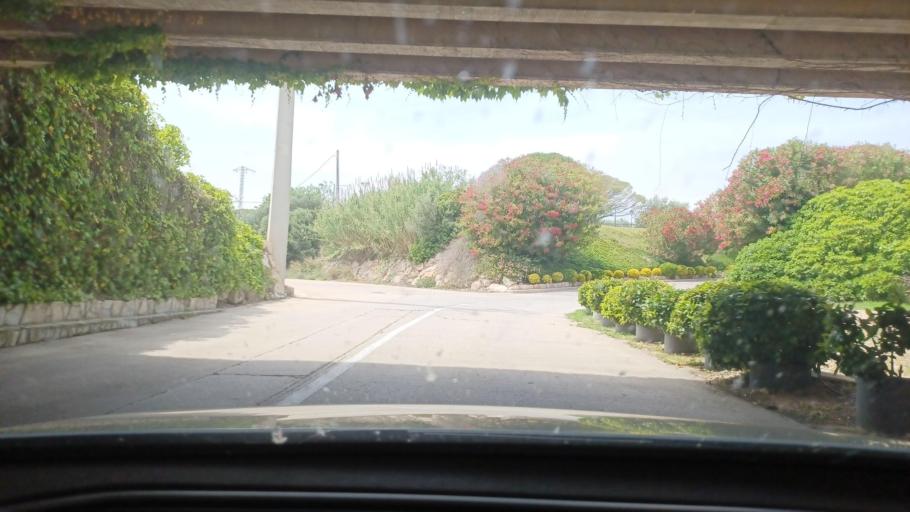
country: ES
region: Catalonia
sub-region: Provincia de Tarragona
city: Vilanova d'Escornalbou
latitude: 41.0334
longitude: 0.9683
